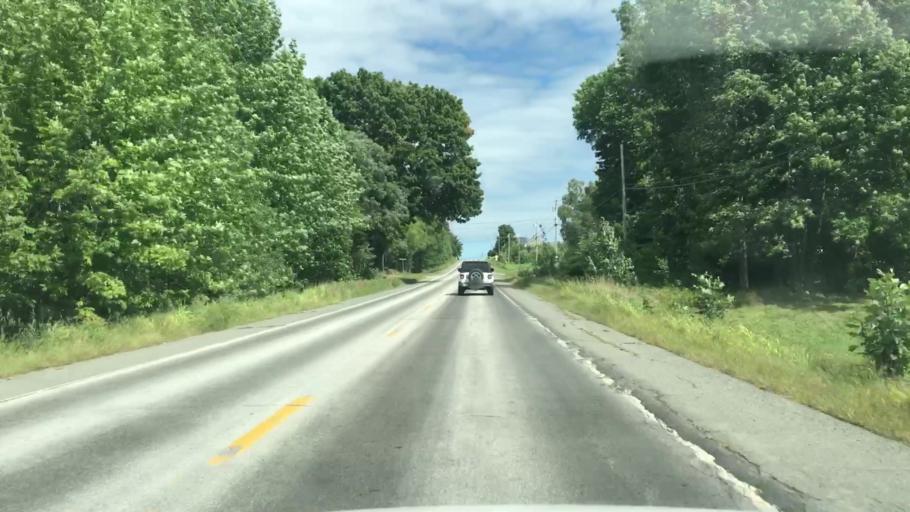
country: US
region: Maine
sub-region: Piscataquis County
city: Dover-Foxcroft
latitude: 45.1596
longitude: -69.2328
